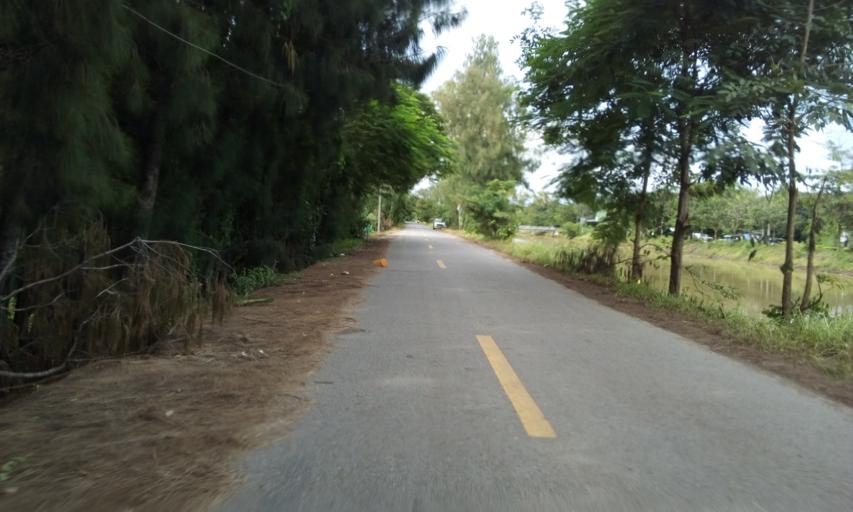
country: TH
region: Pathum Thani
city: Nong Suea
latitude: 14.1162
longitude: 100.8235
